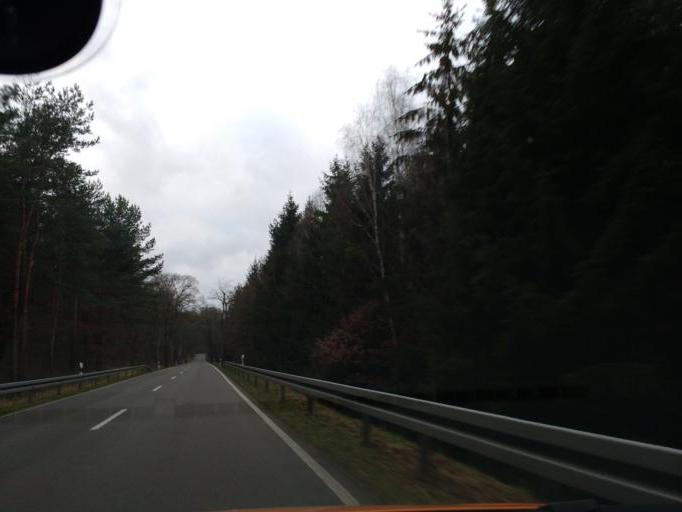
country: DE
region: Brandenburg
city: Strausberg
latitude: 52.6578
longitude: 13.8798
